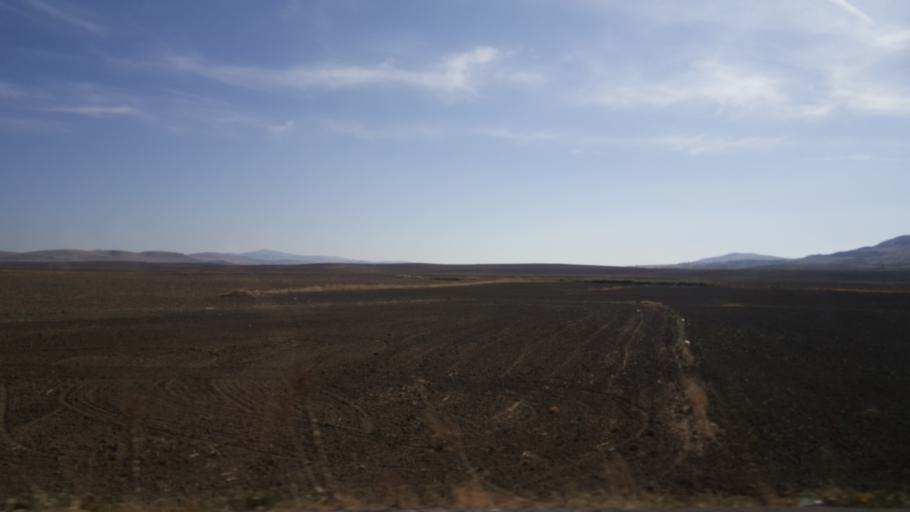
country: TR
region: Ankara
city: Yenice
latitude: 39.3770
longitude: 32.7452
